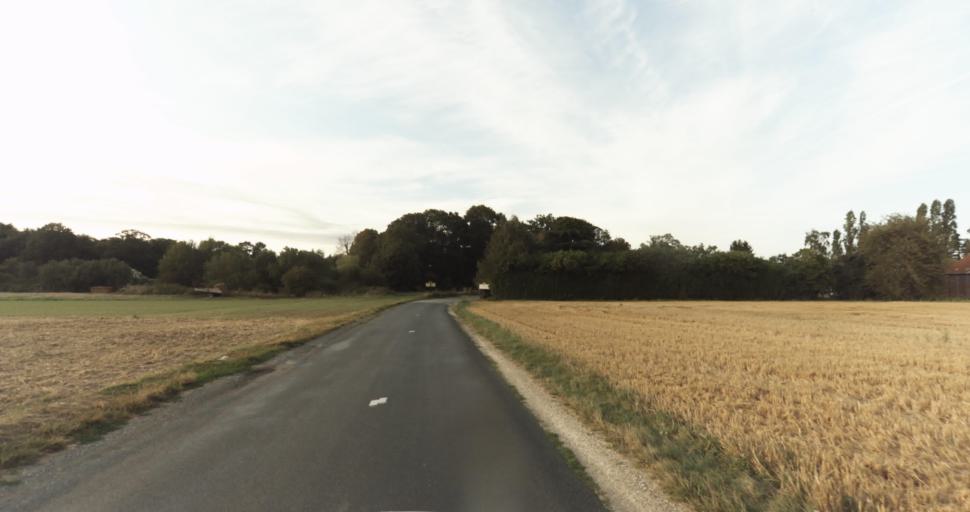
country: FR
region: Haute-Normandie
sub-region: Departement de l'Eure
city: Marcilly-sur-Eure
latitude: 48.8629
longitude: 1.2727
